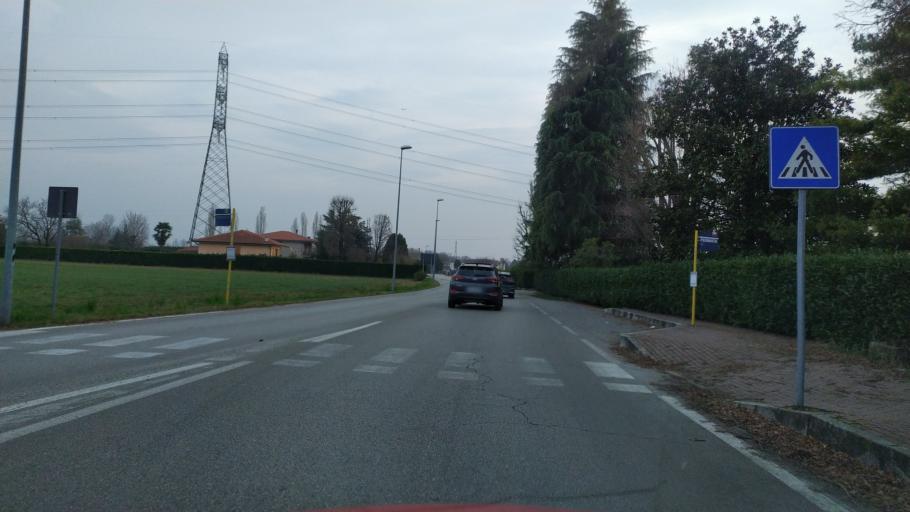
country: IT
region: Veneto
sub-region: Provincia di Vicenza
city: Montecchio Precalcino
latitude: 45.6583
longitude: 11.5581
